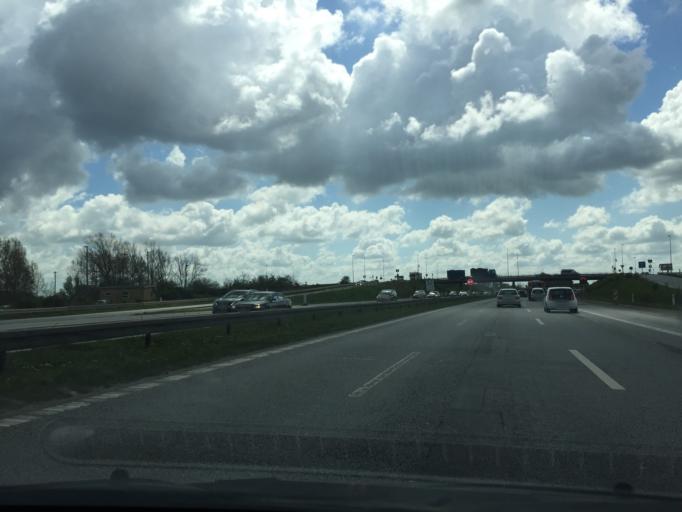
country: DK
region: Zealand
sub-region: Solrod Kommune
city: Solrod
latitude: 55.5198
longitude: 12.1924
